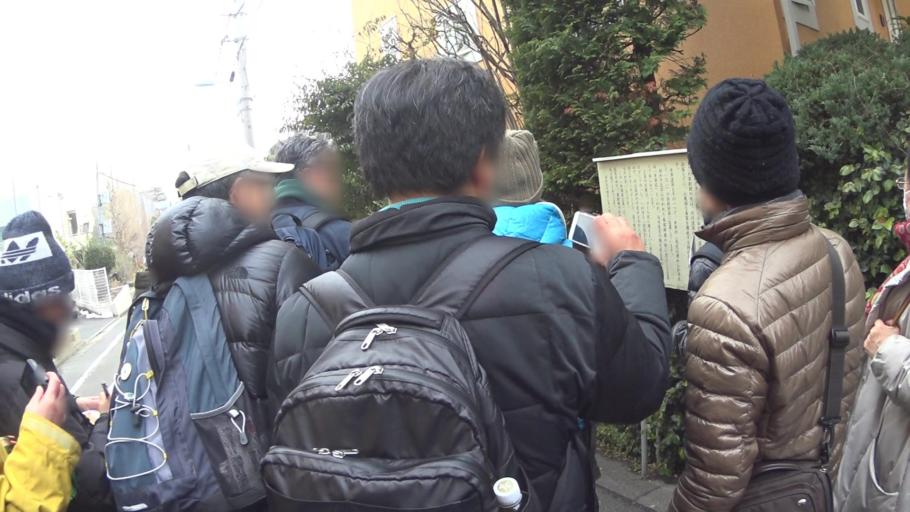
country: JP
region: Tokyo
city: Musashino
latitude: 35.7184
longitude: 139.6021
